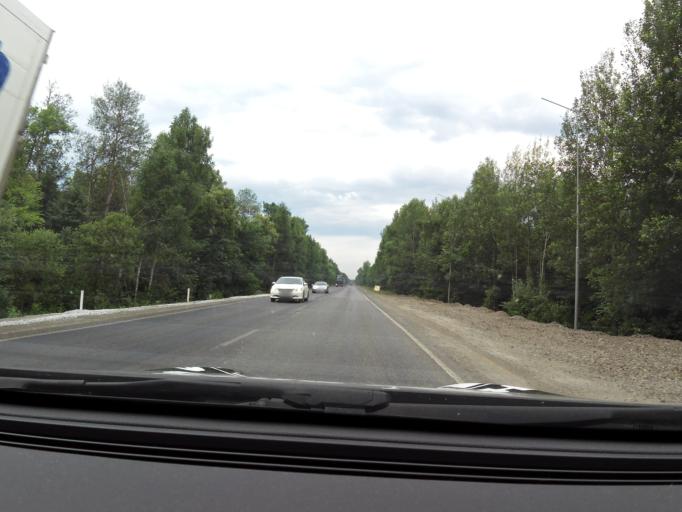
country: RU
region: Bashkortostan
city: Ulu-Telyak
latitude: 54.8323
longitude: 56.9766
